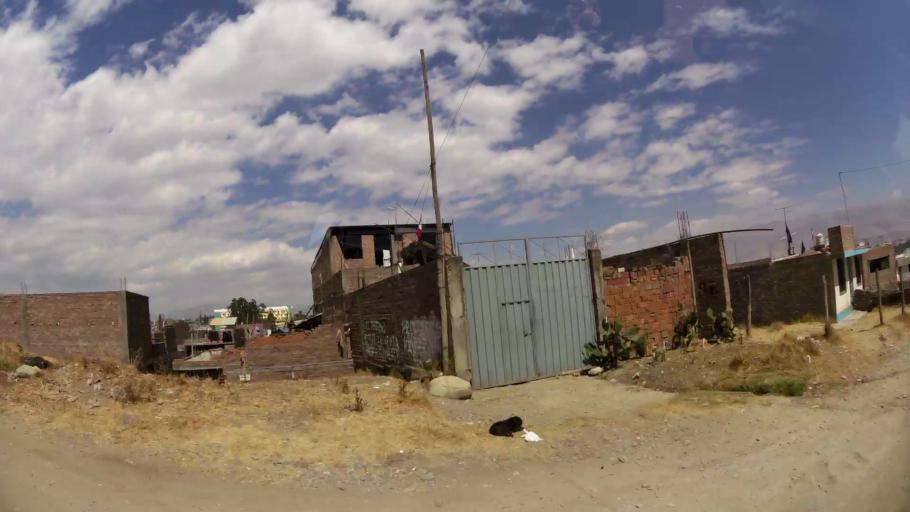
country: PE
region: Junin
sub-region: Provincia de Huancayo
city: El Tambo
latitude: -12.0679
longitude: -75.2244
